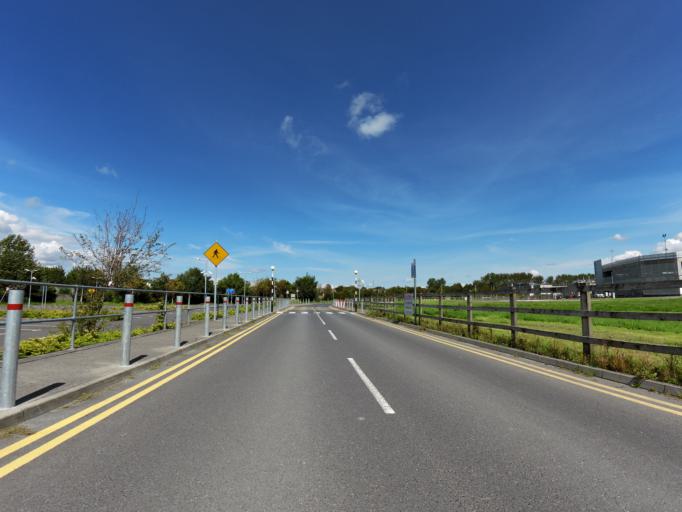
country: IE
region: Connaught
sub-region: County Galway
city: Gaillimh
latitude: 53.2760
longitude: -9.0693
